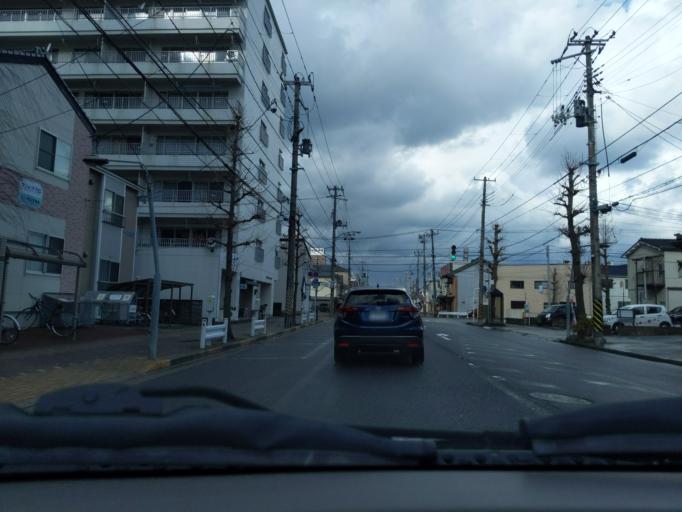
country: JP
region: Niigata
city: Niigata-shi
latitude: 37.9280
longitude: 139.0471
